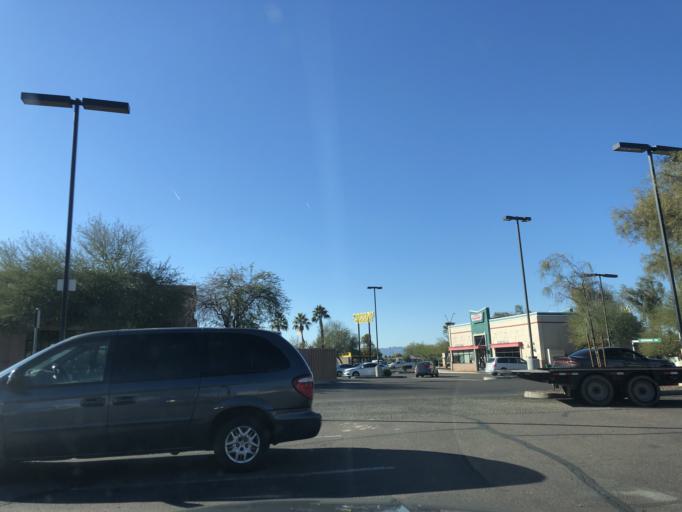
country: US
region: Arizona
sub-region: Maricopa County
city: Avondale
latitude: 33.4548
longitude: -112.3397
